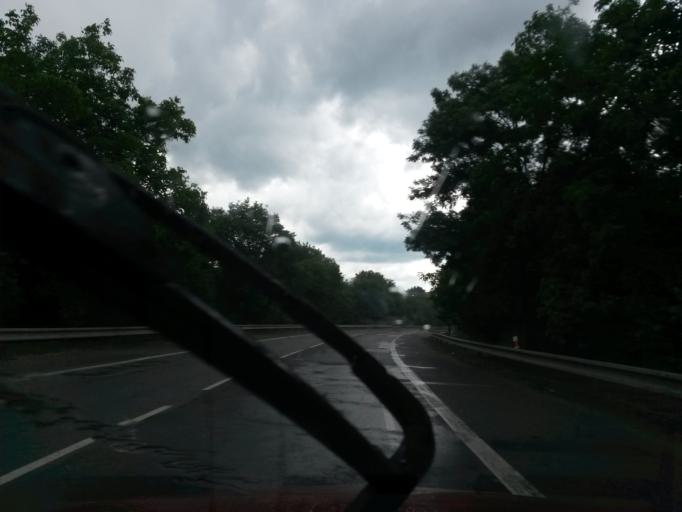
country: SK
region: Presovsky
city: Vranov nad Topl'ou
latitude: 48.8554
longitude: 21.7483
